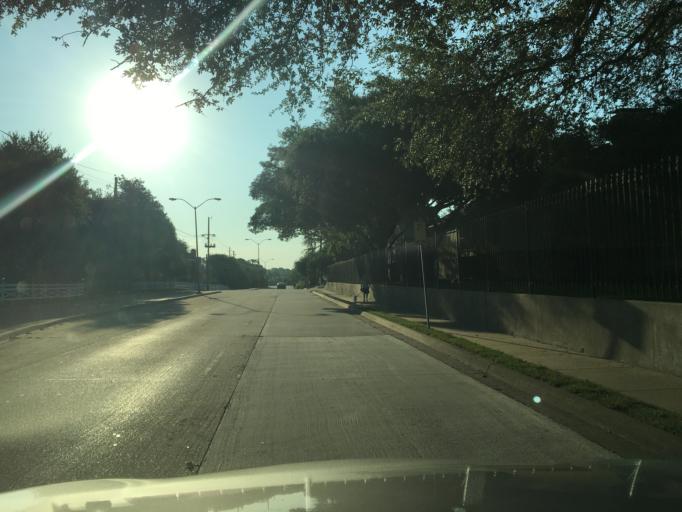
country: US
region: Texas
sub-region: Dallas County
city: Addison
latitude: 32.9685
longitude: -96.8167
